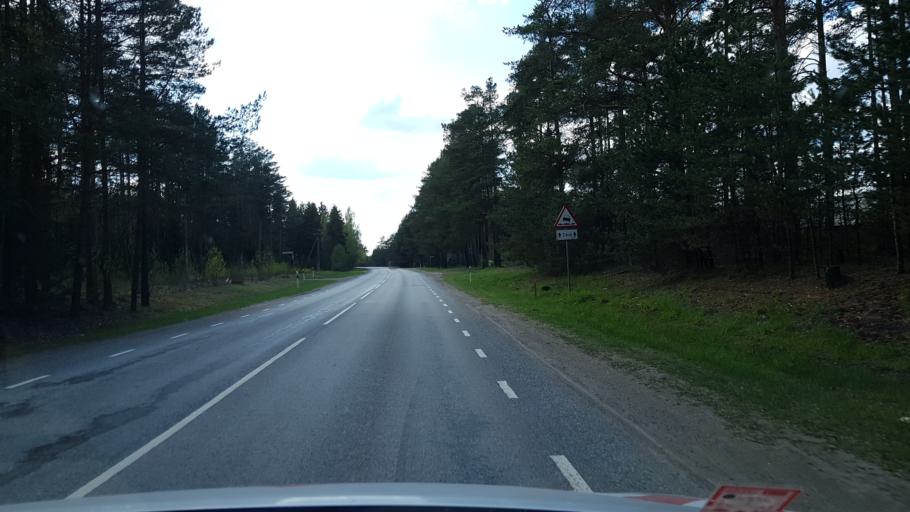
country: EE
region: Tartu
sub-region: UElenurme vald
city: Ulenurme
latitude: 58.3269
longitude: 26.7788
